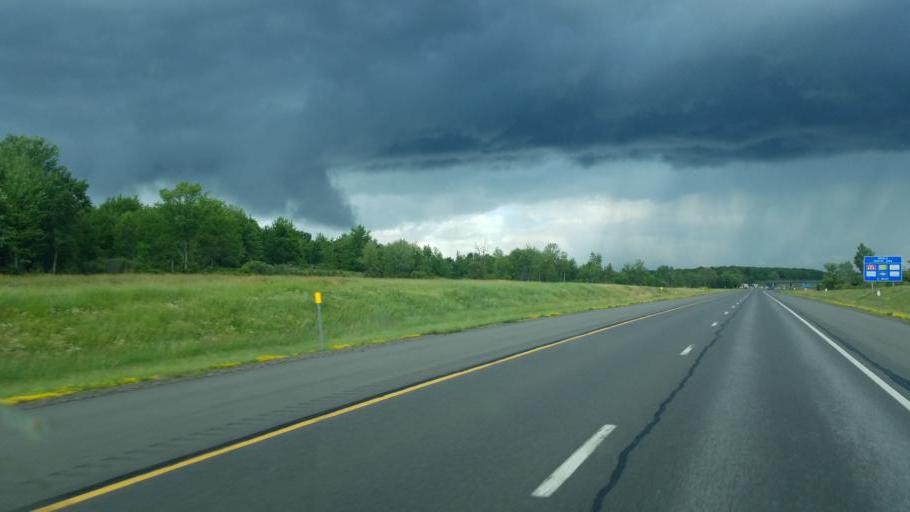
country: US
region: New York
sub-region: Erie County
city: Angola
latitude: 42.6073
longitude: -79.0238
